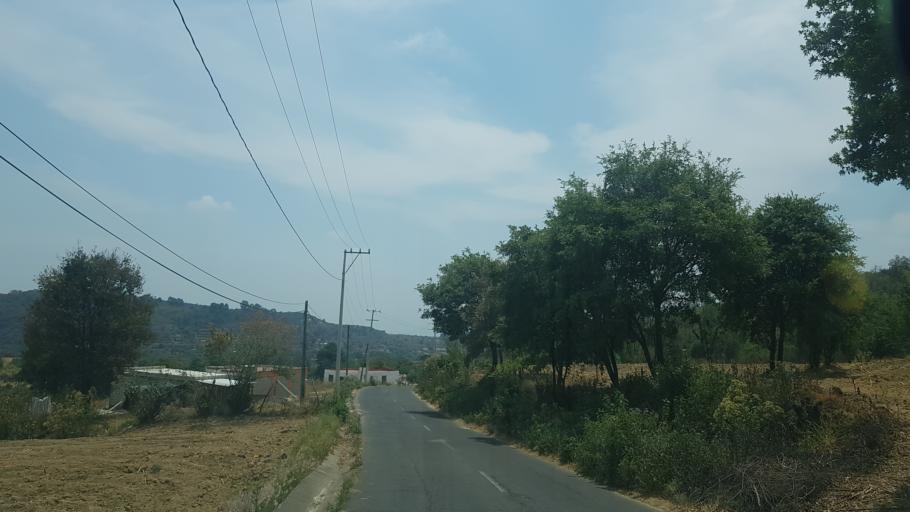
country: MX
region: Puebla
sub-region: Tochimilco
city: Santa Cruz Cuautomatitla
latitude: 18.8746
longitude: -98.6183
